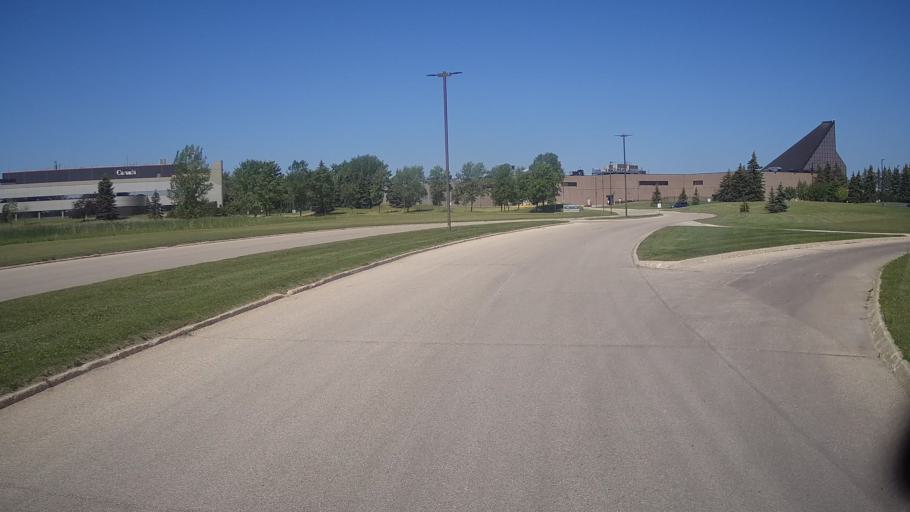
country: CA
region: Manitoba
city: Winnipeg
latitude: 49.8510
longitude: -97.0510
